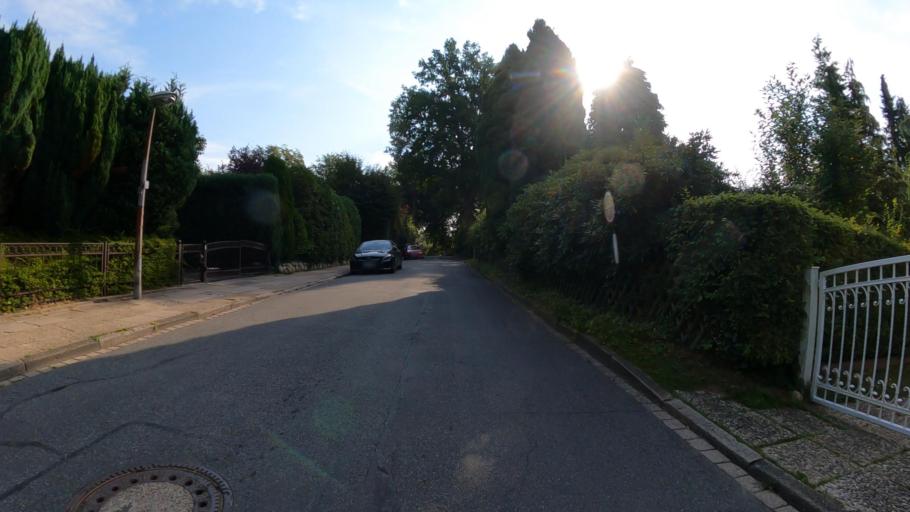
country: DE
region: Schleswig-Holstein
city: Wentorf bei Hamburg
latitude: 53.4988
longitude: 10.2487
